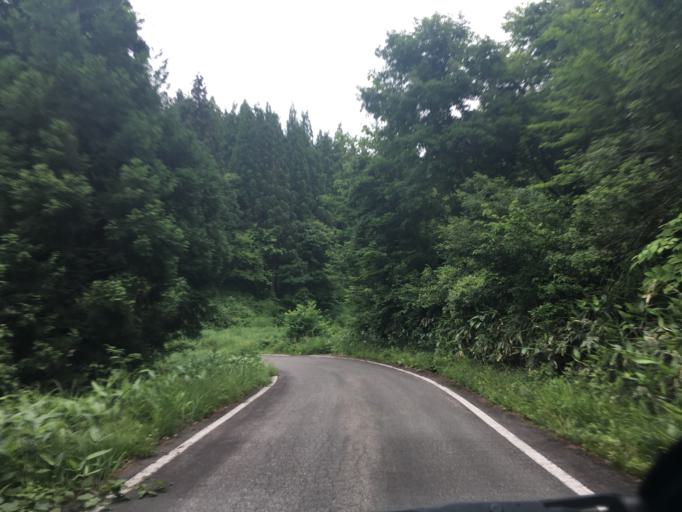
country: JP
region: Fukushima
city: Kitakata
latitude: 37.4791
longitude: 139.7504
